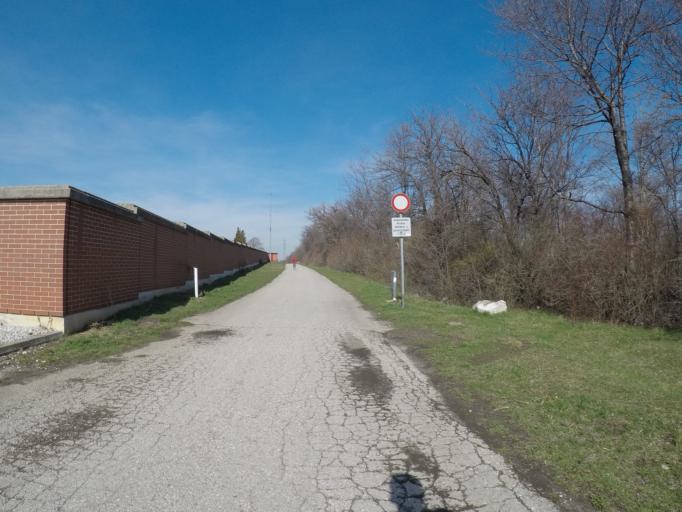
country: AT
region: Lower Austria
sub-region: Politischer Bezirk Modling
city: Vosendorf
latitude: 48.1251
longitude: 16.3426
